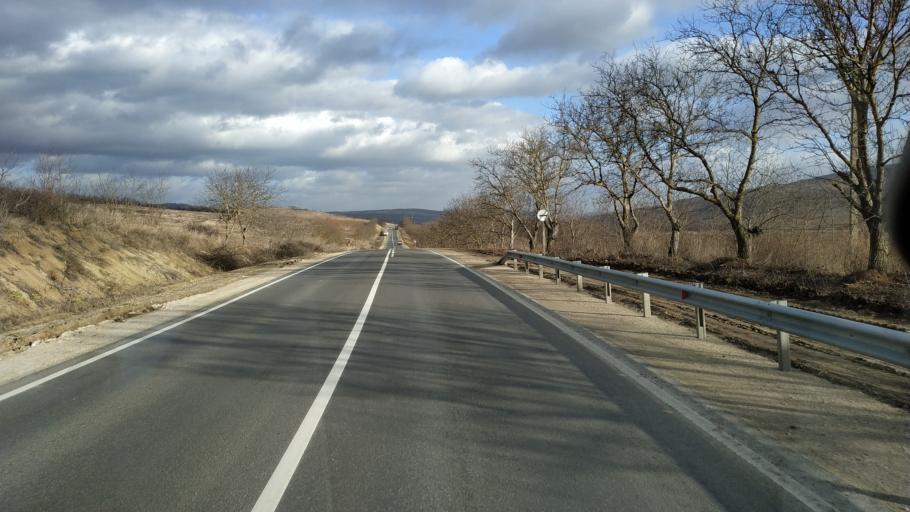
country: MD
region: Calarasi
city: Calarasi
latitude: 47.2970
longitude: 28.1534
